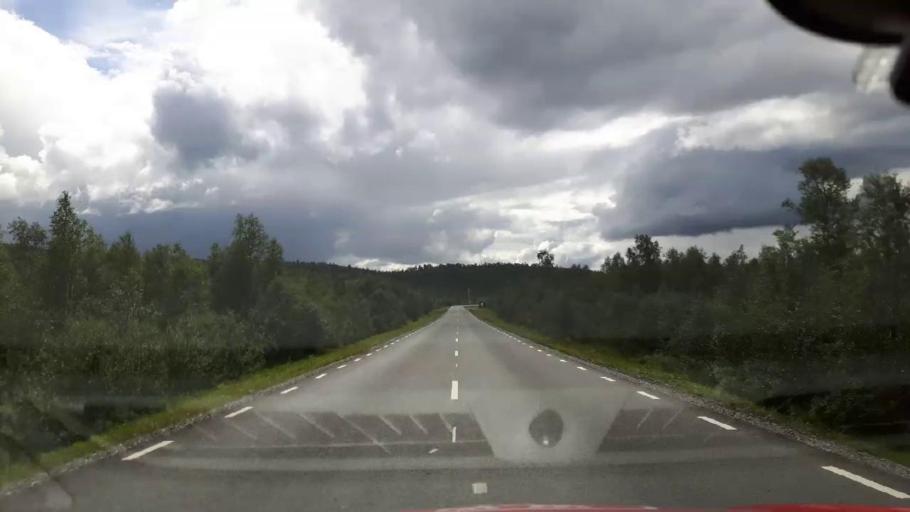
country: NO
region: Nordland
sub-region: Hattfjelldal
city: Hattfjelldal
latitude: 64.9824
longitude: 14.2129
